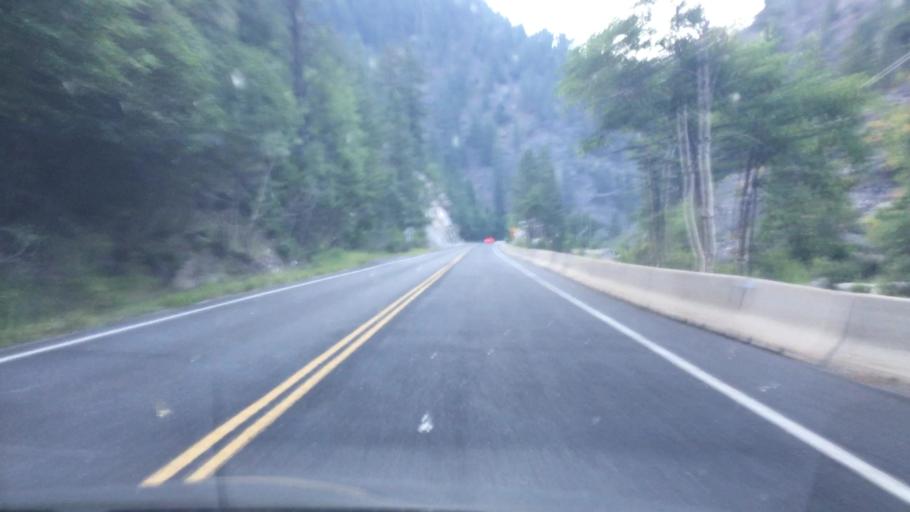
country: US
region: Idaho
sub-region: Valley County
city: McCall
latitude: 45.1401
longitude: -116.2871
